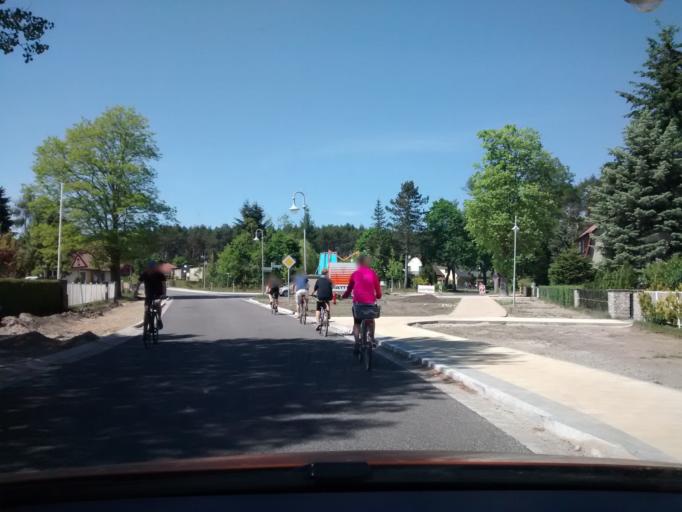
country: DE
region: Brandenburg
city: Wendisch Rietz
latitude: 52.2181
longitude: 14.0056
